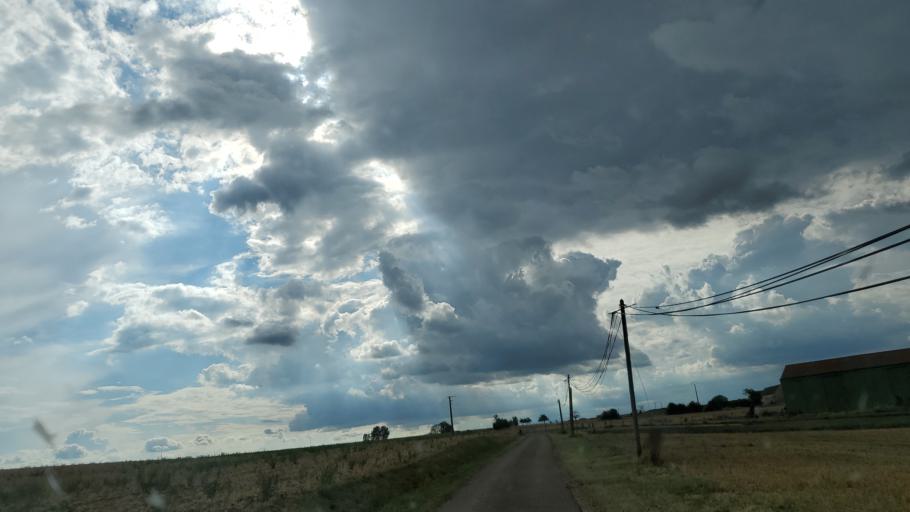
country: FR
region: Ile-de-France
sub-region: Departement de Seine-et-Marne
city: Chailly-en-Brie
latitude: 48.7739
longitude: 3.1626
